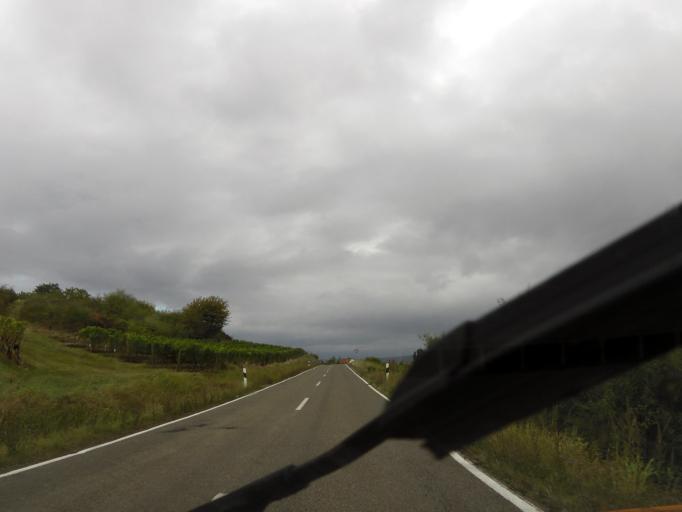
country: DE
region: Rheinland-Pfalz
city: Wonsheim
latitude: 49.7924
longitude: 7.9594
